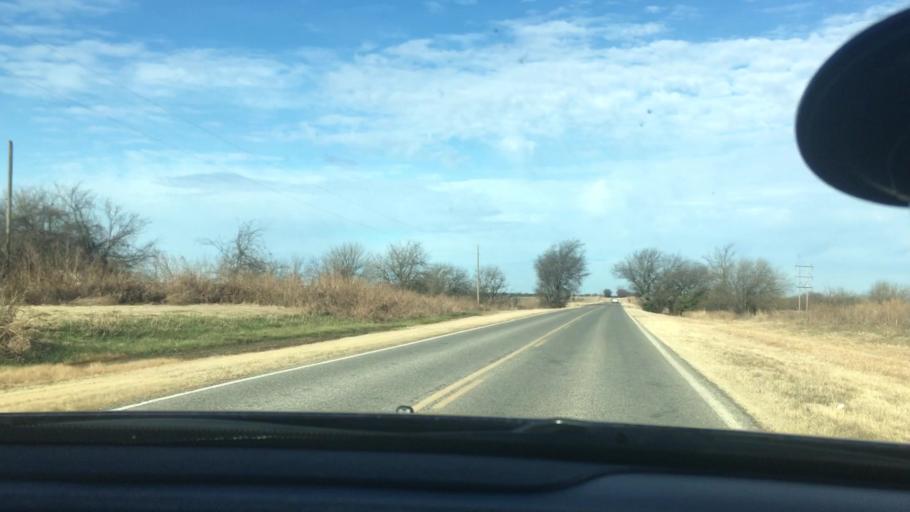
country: US
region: Oklahoma
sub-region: Seminole County
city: Konawa
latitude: 34.9718
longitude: -96.7790
